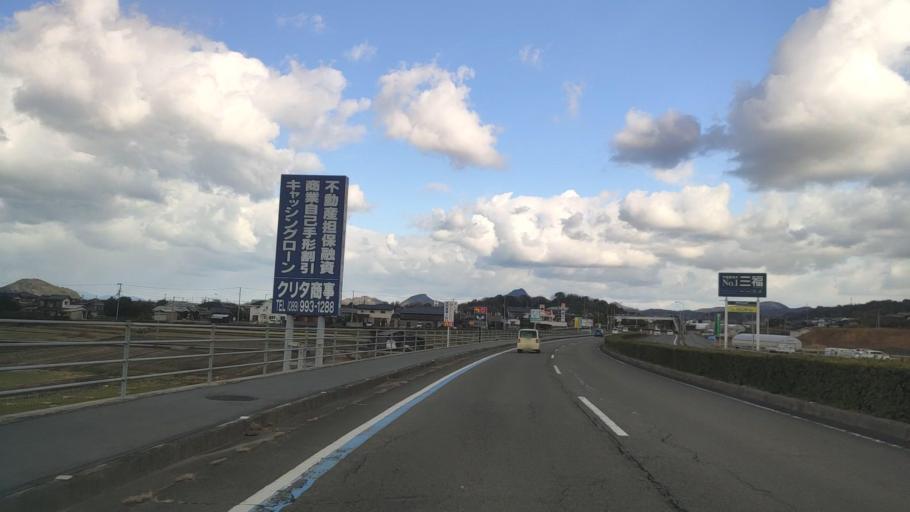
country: JP
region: Ehime
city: Hojo
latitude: 33.9410
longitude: 132.7741
